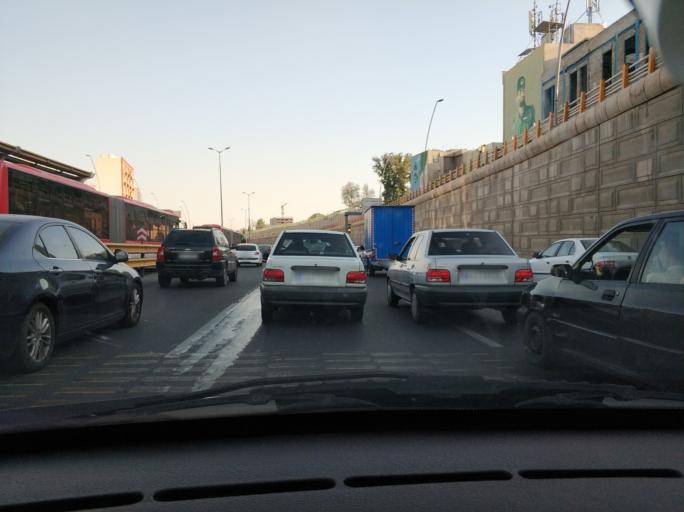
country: IR
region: Tehran
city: Tehran
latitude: 35.6965
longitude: 51.4567
